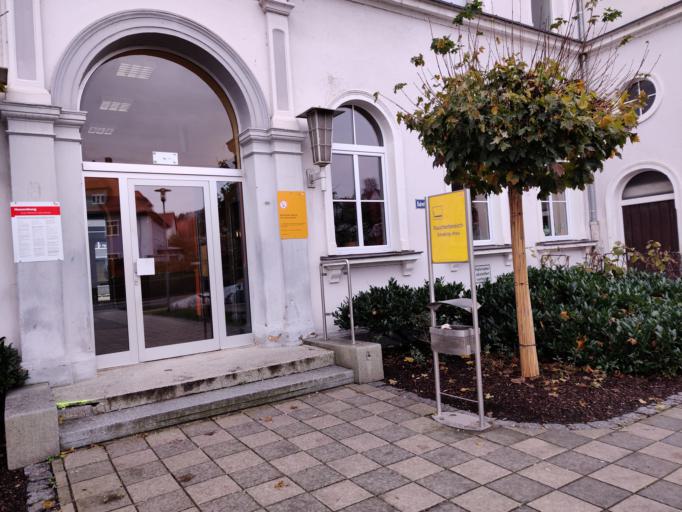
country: DE
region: Bavaria
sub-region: Upper Palatinate
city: Cham
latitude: 49.2222
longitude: 12.6571
